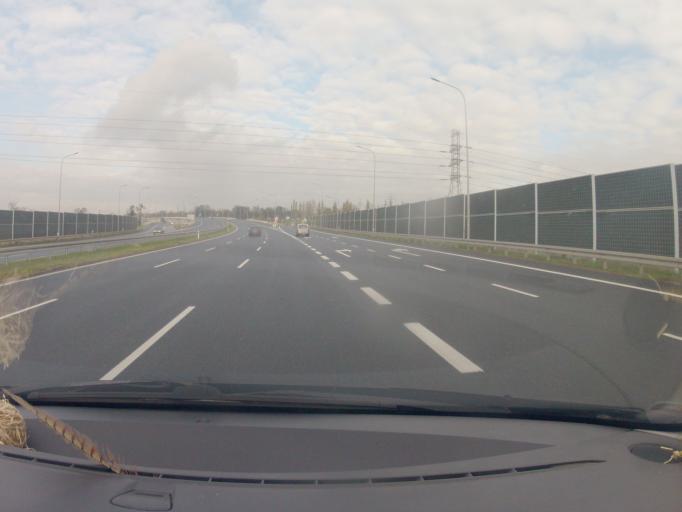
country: PL
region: Lesser Poland Voivodeship
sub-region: Powiat wielicki
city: Kokotow
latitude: 50.0607
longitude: 20.0751
